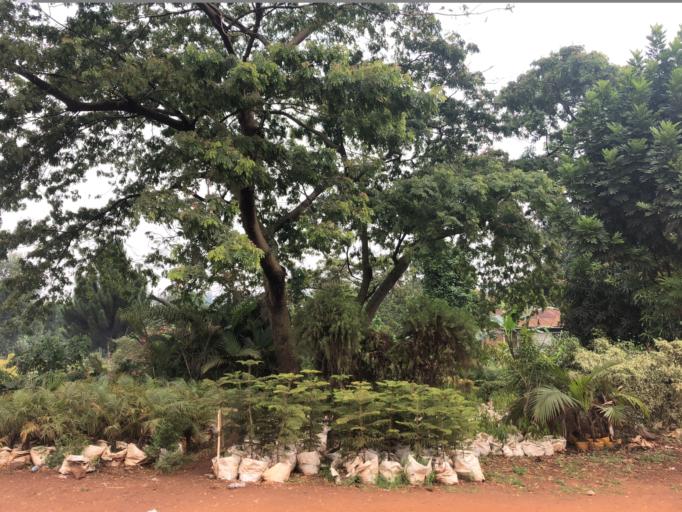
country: UG
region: Central Region
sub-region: Mukono District
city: Mukono
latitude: 0.3651
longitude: 32.7416
